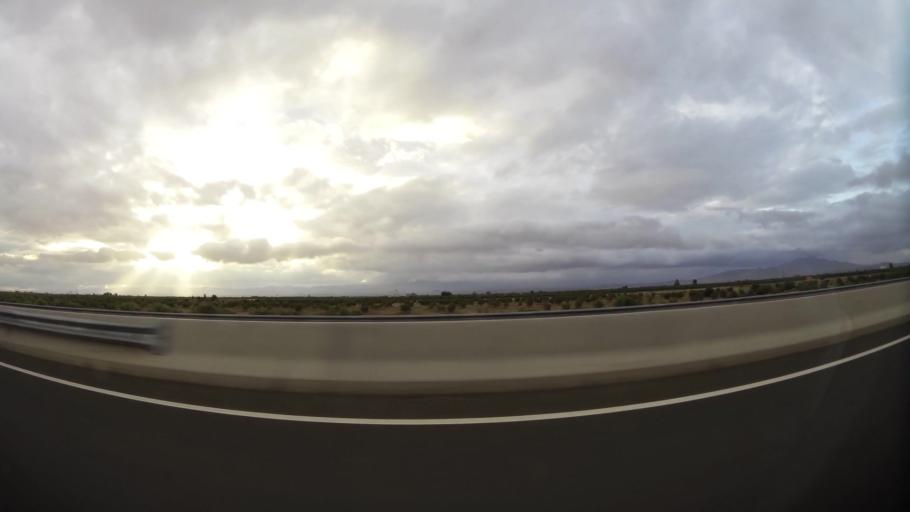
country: MA
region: Taza-Al Hoceima-Taounate
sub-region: Taza
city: Guercif
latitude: 34.3485
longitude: -3.3155
